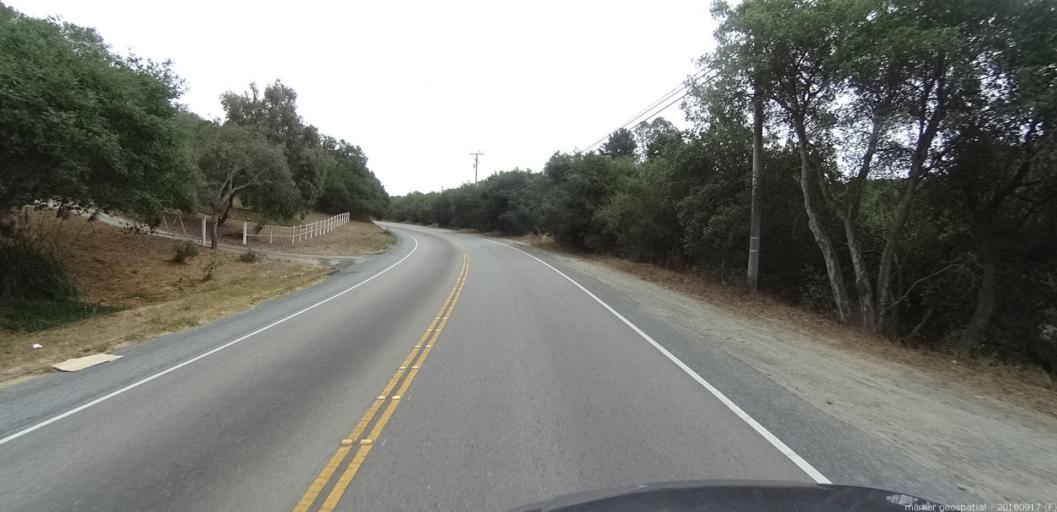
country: US
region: California
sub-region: Monterey County
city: Prunedale
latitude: 36.8038
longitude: -121.6790
